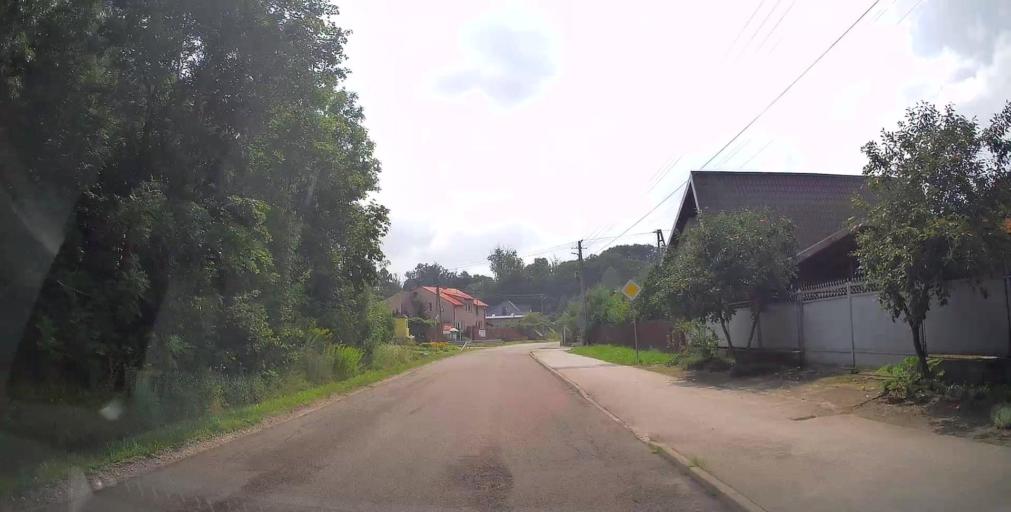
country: PL
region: Masovian Voivodeship
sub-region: Powiat bialobrzeski
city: Sucha
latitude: 51.6236
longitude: 20.9528
